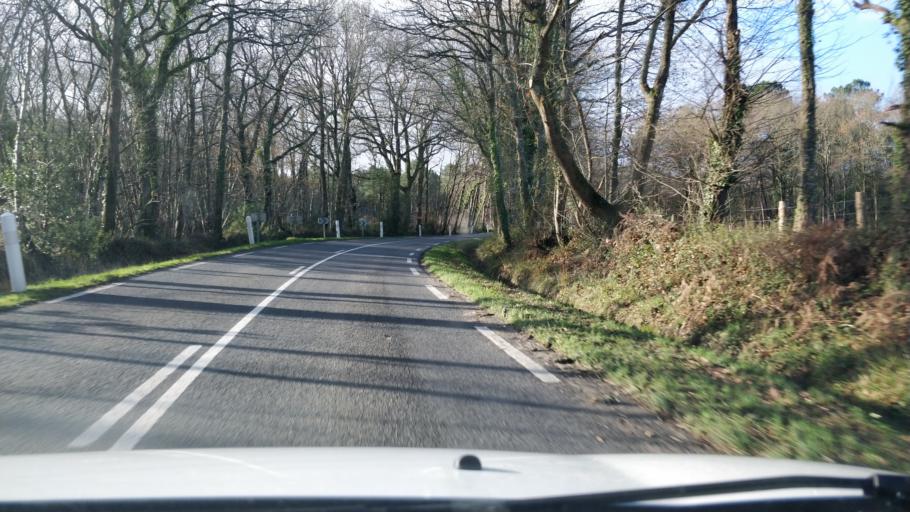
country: FR
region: Pays de la Loire
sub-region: Departement de la Loire-Atlantique
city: Herbignac
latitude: 47.4368
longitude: -2.3401
